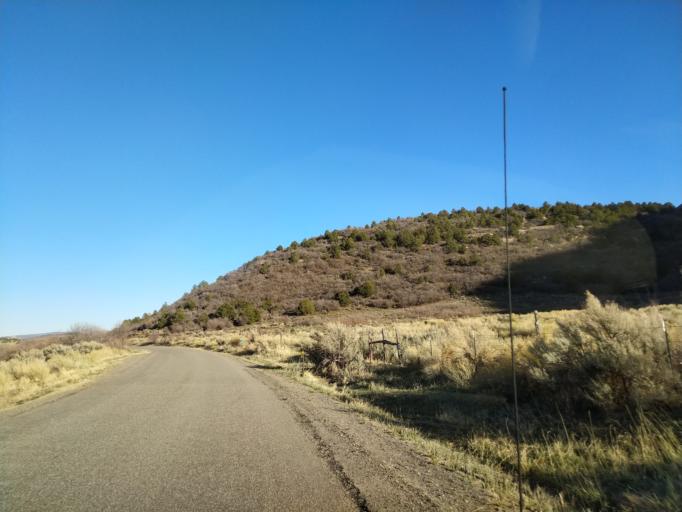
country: US
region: Colorado
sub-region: Mesa County
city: Loma
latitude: 38.9522
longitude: -108.9923
